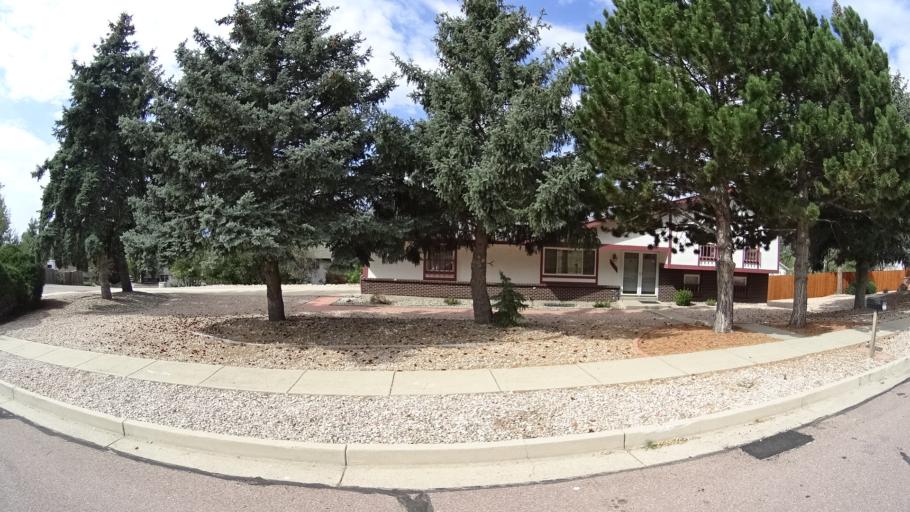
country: US
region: Colorado
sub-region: El Paso County
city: Cimarron Hills
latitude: 38.8513
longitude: -104.7273
